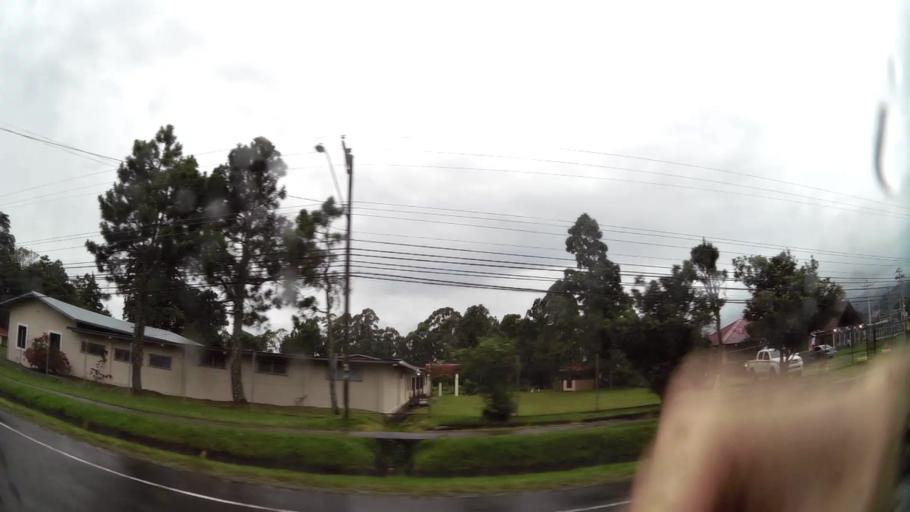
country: PA
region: Chiriqui
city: Volcan
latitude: 8.7785
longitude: -82.6396
